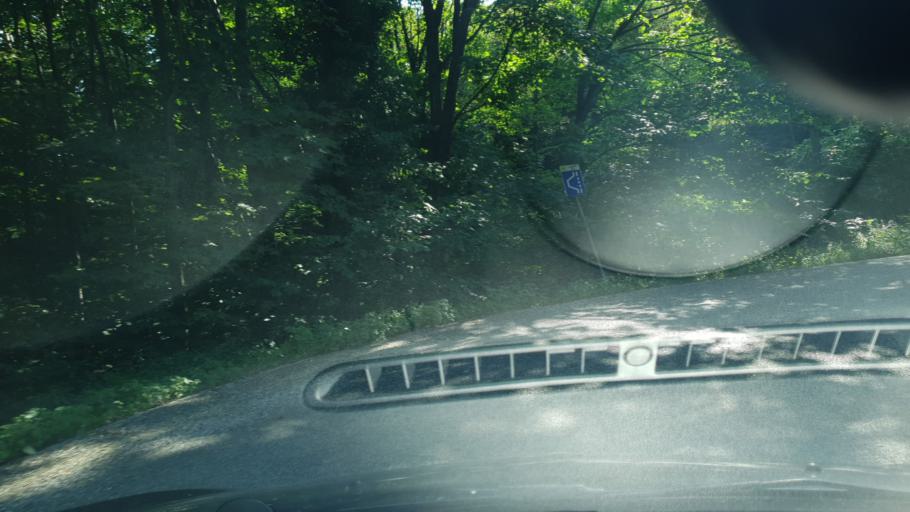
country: HR
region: Grad Zagreb
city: Kasina
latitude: 45.8806
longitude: 15.9732
